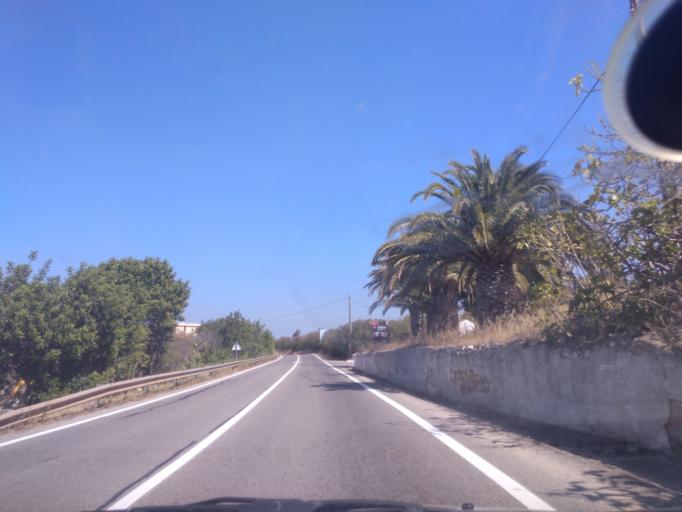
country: PT
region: Faro
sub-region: Lagos
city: Lagos
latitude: 37.1143
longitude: -8.6860
